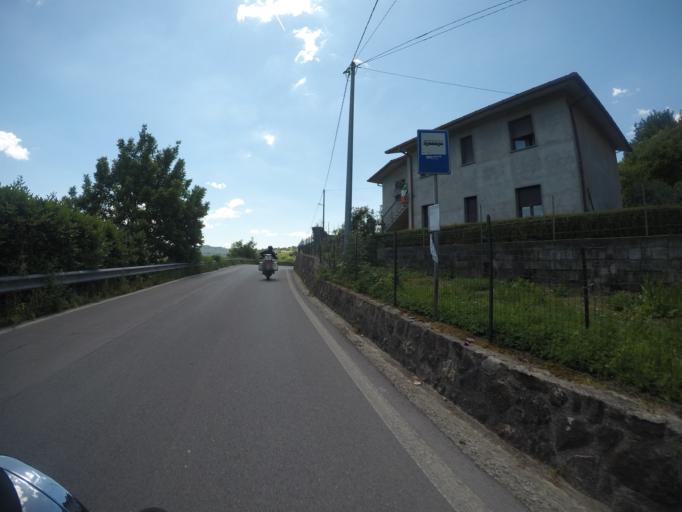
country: IT
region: Tuscany
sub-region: Provincia di Lucca
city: San Romano in Garfagnana
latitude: 44.1387
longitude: 10.3666
